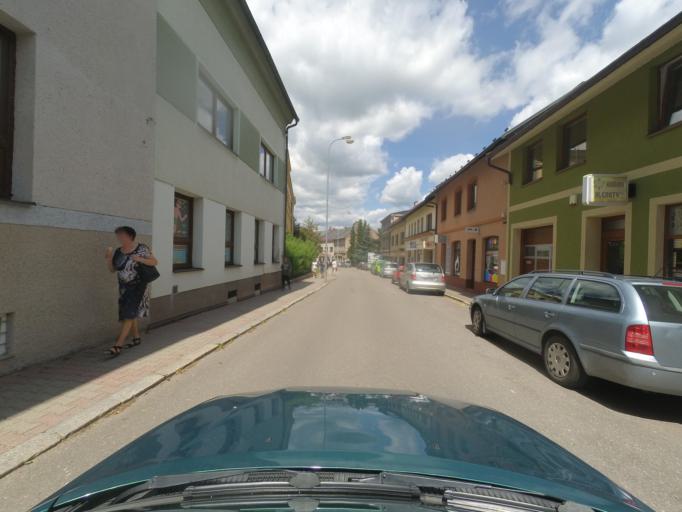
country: CZ
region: Pardubicky
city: Zamberk
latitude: 50.0850
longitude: 16.4650
